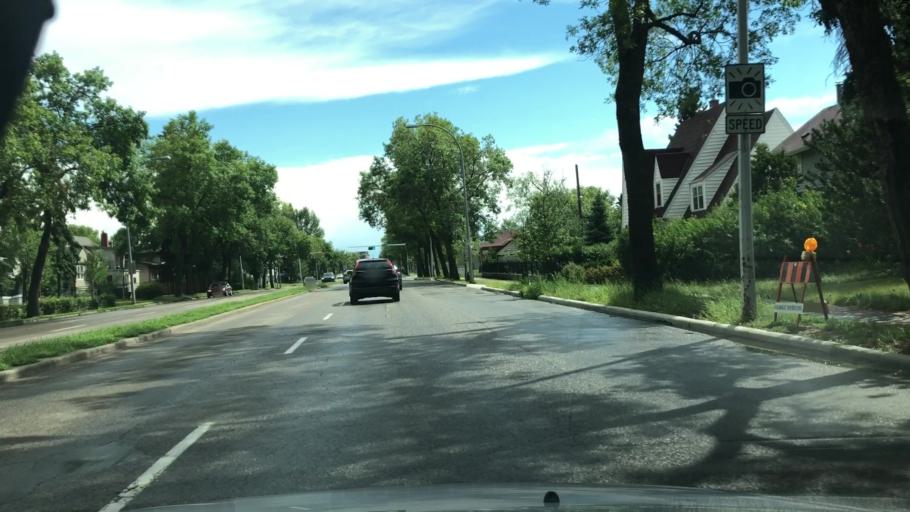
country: CA
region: Alberta
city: Edmonton
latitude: 53.5582
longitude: -113.5085
